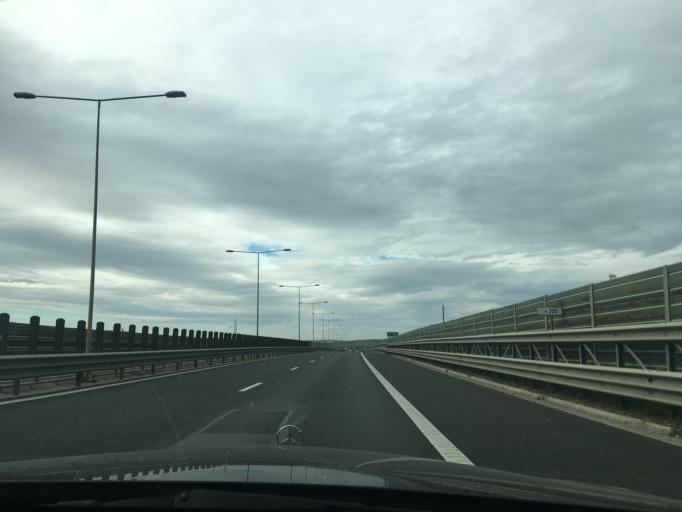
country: RO
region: Sibiu
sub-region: Municipiul Sibiu
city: Sibiu
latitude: 45.8074
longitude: 24.1762
